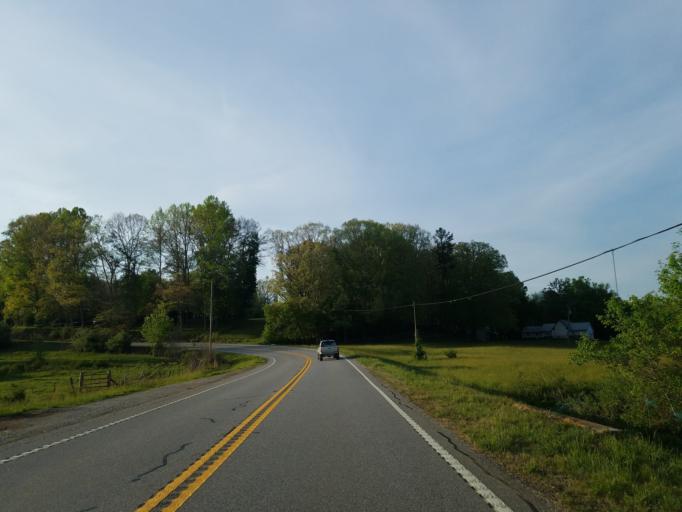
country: US
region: Georgia
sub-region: Fannin County
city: Blue Ridge
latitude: 34.8373
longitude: -84.1900
